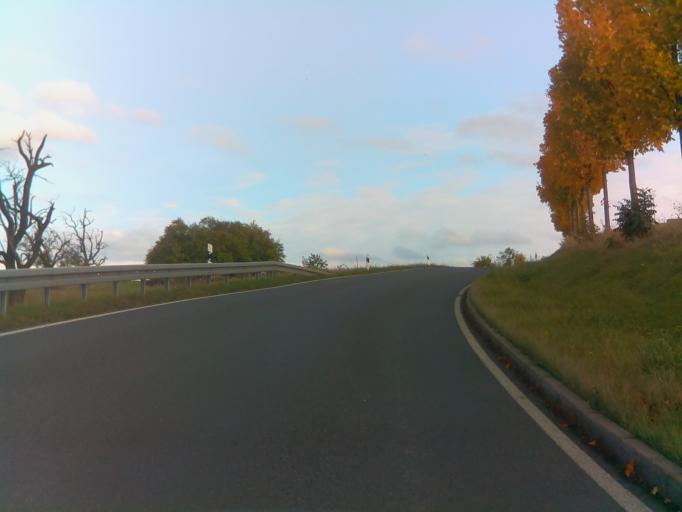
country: DE
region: Thuringia
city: Alkersleben
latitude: 50.8478
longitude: 11.0465
